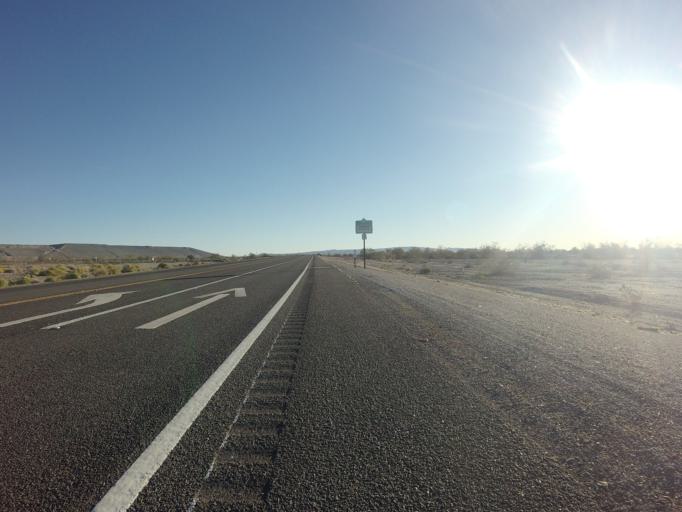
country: MX
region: Baja California
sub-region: Mexicali
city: Ejido Netzahualcoyotl
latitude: 33.0163
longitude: -114.9916
